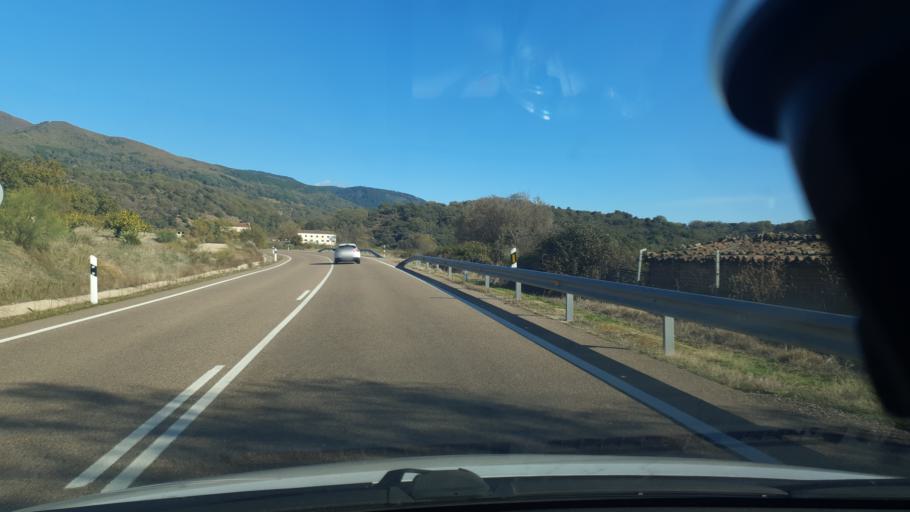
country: ES
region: Castille and Leon
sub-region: Provincia de Avila
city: Poyales del Hoyo
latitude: 40.1476
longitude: -5.1912
